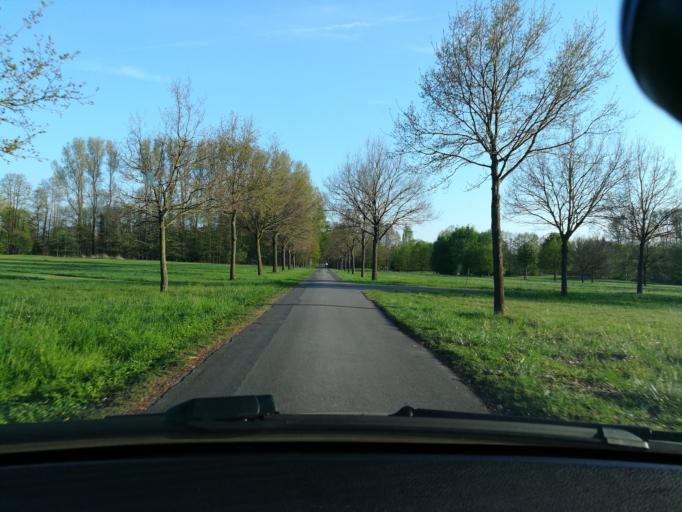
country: DE
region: North Rhine-Westphalia
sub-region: Regierungsbezirk Munster
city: Sassenberg
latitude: 52.0193
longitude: 8.0928
